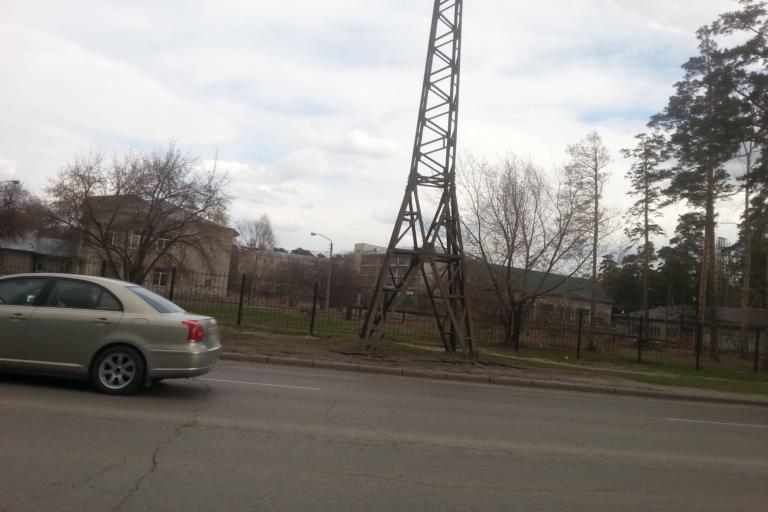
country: RU
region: Altai Krai
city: Zaton
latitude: 53.2824
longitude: 83.7500
